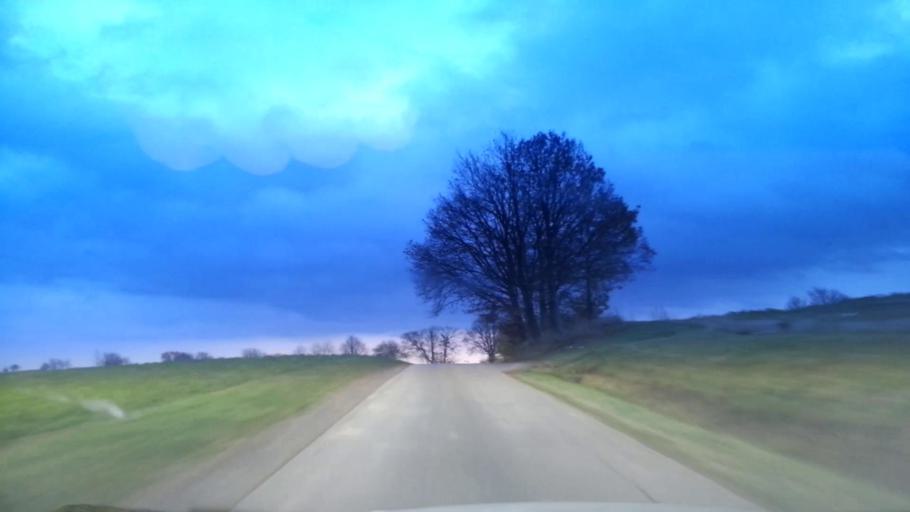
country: DE
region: Bavaria
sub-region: Upper Palatinate
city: Fuchsmuhl
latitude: 49.9206
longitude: 12.1633
